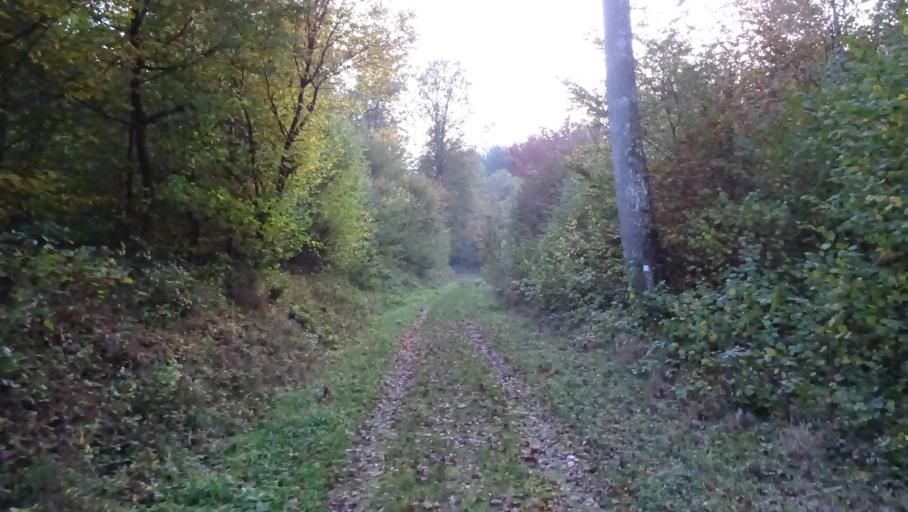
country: DE
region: Baden-Wuerttemberg
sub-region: Karlsruhe Region
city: Neckargerach
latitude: 49.3811
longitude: 9.0888
